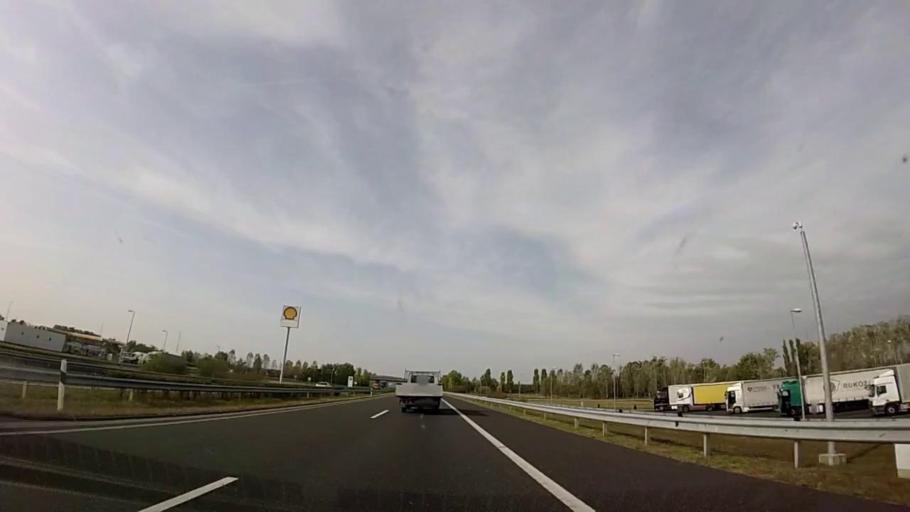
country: HU
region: Somogy
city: Kethely
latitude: 46.6845
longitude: 17.3794
